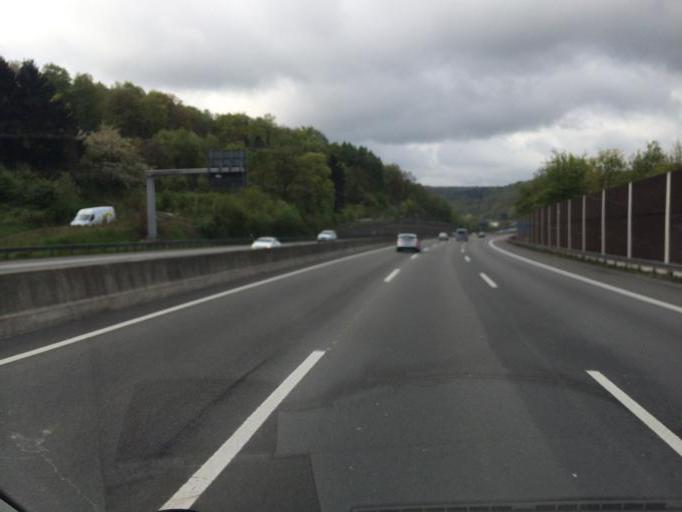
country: DE
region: North Rhine-Westphalia
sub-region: Regierungsbezirk Arnsberg
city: Schwelm
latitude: 51.2616
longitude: 7.2398
